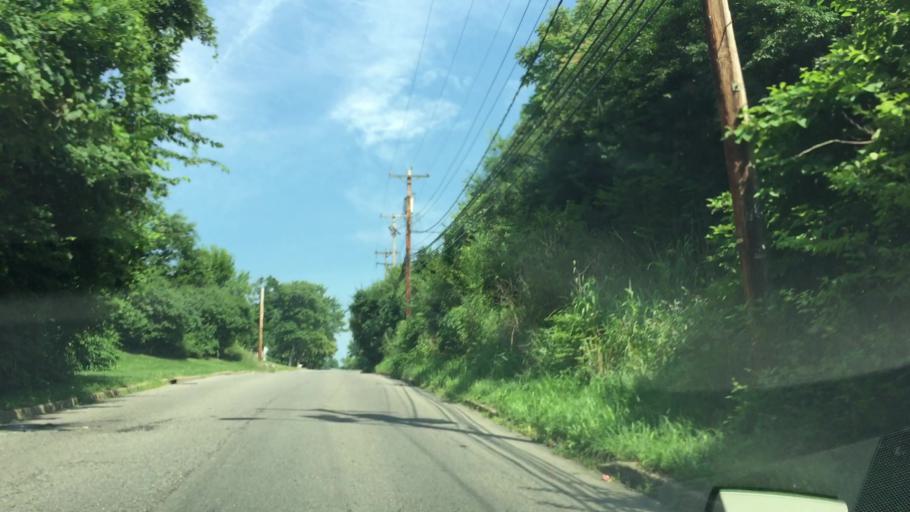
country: US
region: Pennsylvania
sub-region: Allegheny County
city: Carnegie
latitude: 40.4159
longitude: -80.0873
